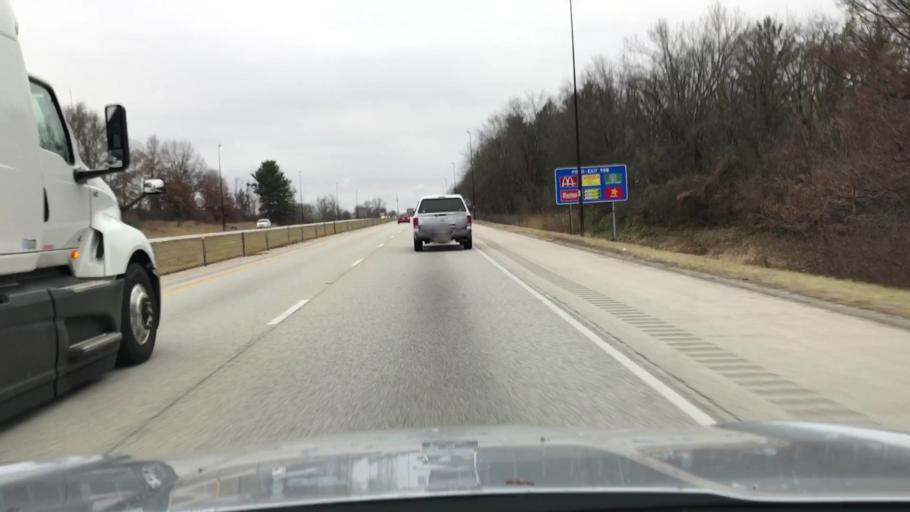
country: US
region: Illinois
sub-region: Sangamon County
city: Grandview
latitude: 39.8190
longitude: -89.5930
